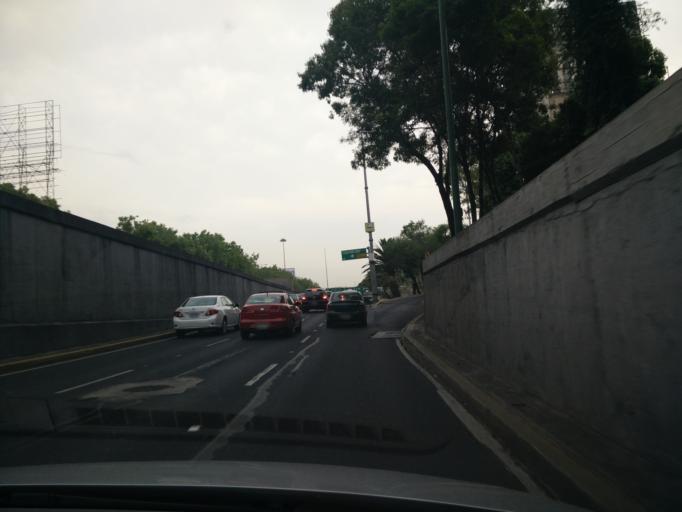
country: MX
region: Mexico City
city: Benito Juarez
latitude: 19.4034
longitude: -99.1380
